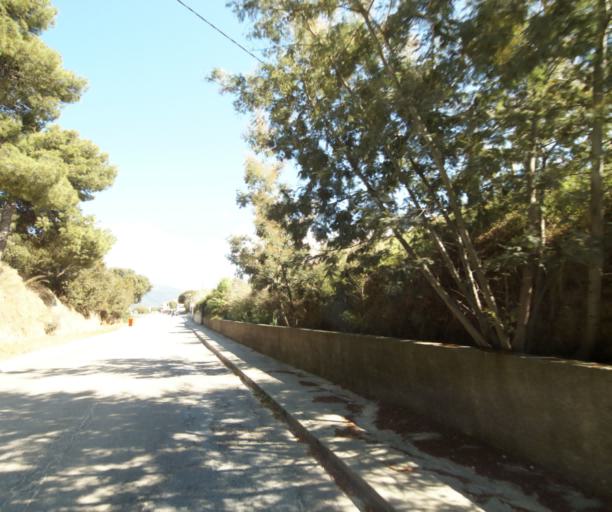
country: FR
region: Corsica
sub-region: Departement de la Corse-du-Sud
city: Propriano
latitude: 41.6703
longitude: 8.9188
